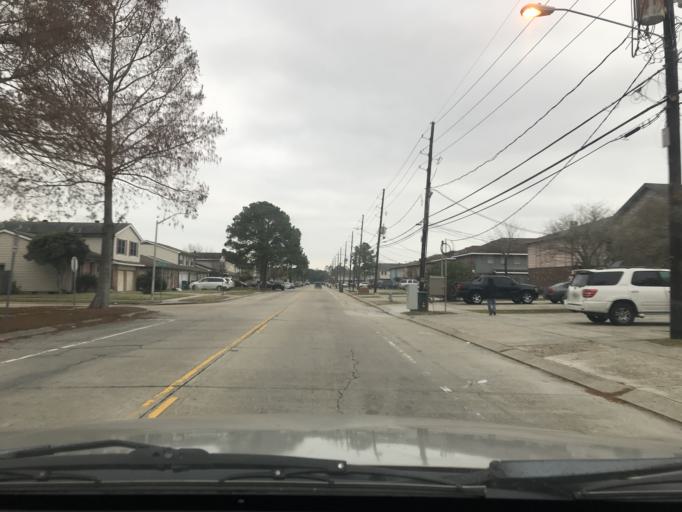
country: US
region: Louisiana
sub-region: Jefferson Parish
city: Woodmere
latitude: 29.8641
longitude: -90.0759
